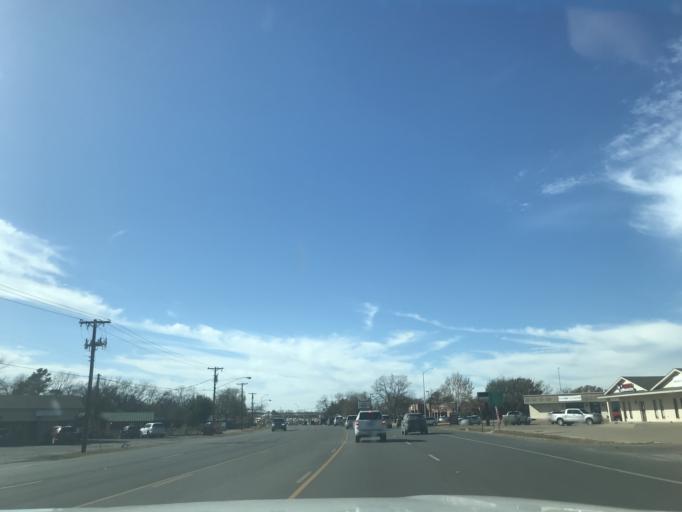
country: US
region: Texas
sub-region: Erath County
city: Stephenville
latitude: 32.2073
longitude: -98.2242
